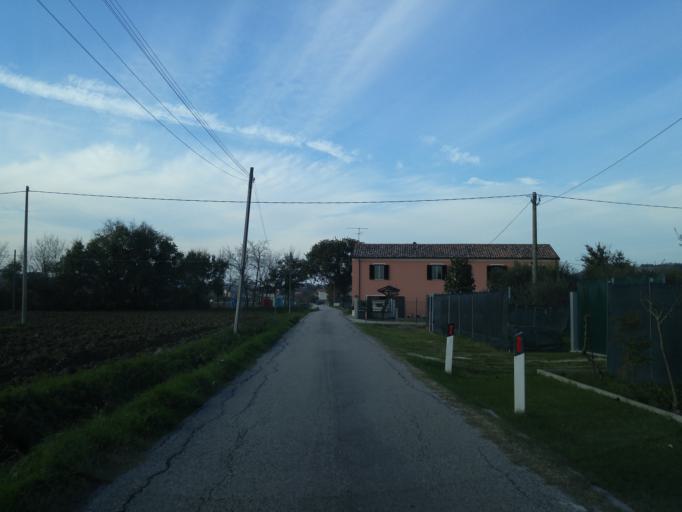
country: IT
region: The Marches
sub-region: Provincia di Pesaro e Urbino
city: Cuccurano
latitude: 43.7887
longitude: 12.9610
